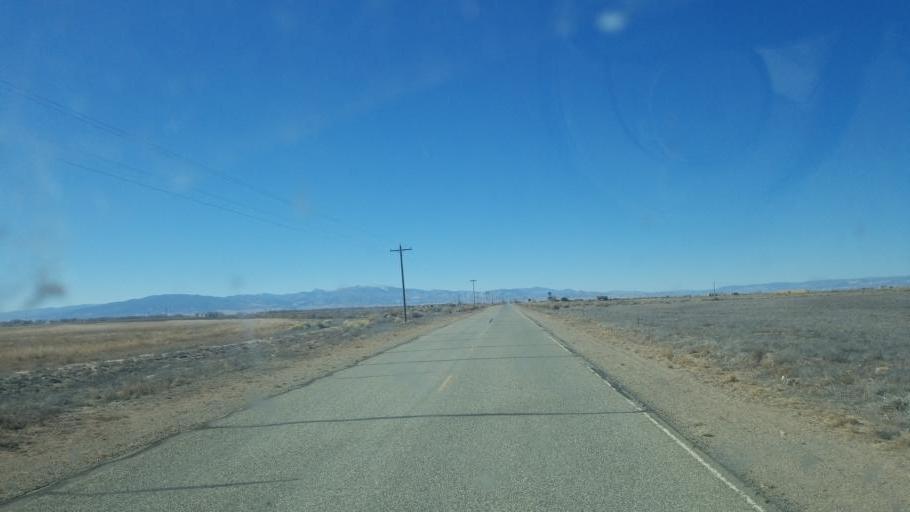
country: US
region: Colorado
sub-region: Alamosa County
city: Alamosa
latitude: 37.5745
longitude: -105.9239
